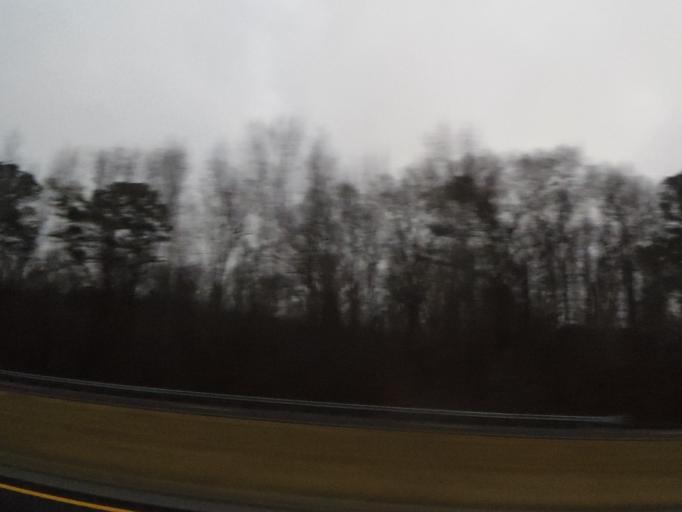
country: US
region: Alabama
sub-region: Cullman County
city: Cullman
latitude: 34.2530
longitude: -86.8905
